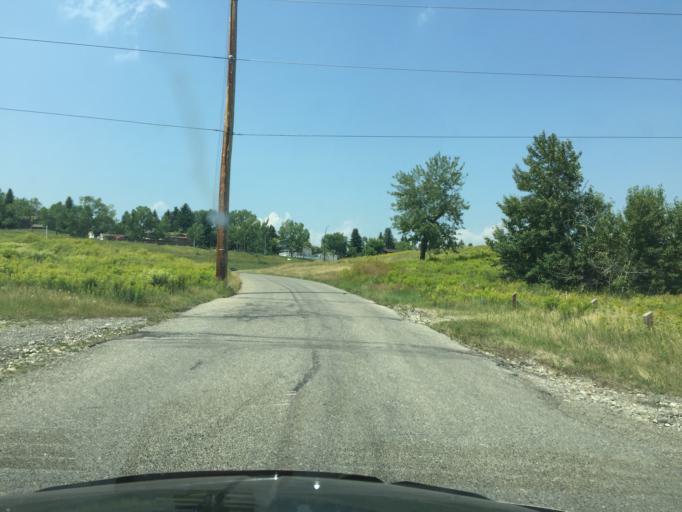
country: CA
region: Alberta
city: Calgary
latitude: 50.9155
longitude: -114.0143
